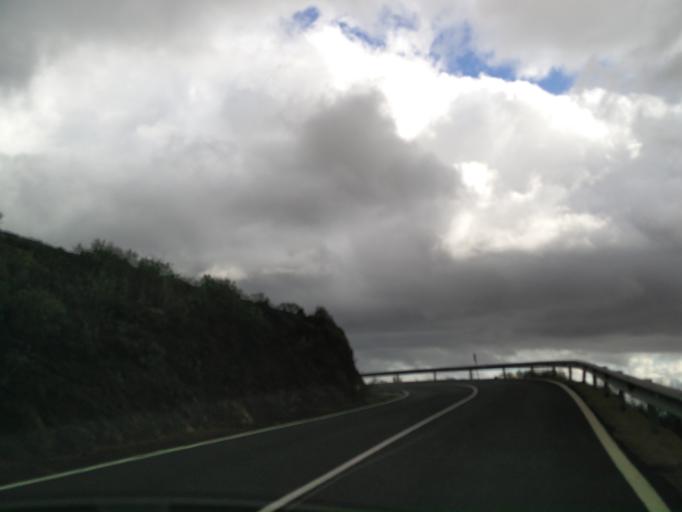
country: ES
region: Canary Islands
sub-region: Provincia de Santa Cruz de Tenerife
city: Arona
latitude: 28.1176
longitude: -16.6779
